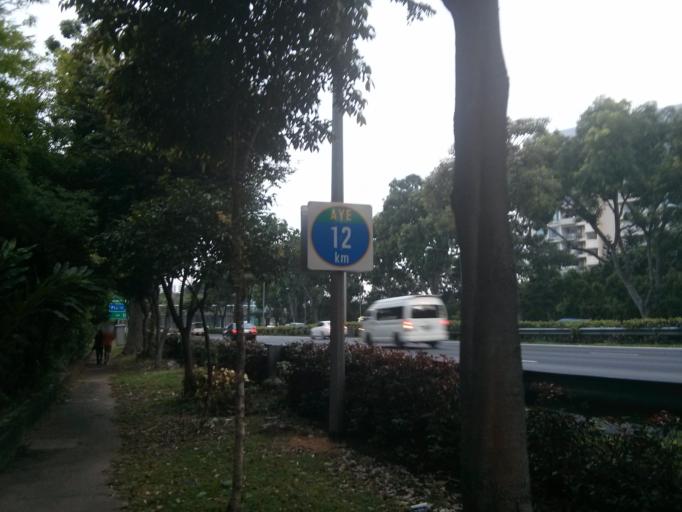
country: SG
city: Singapore
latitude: 1.3193
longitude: 103.7563
